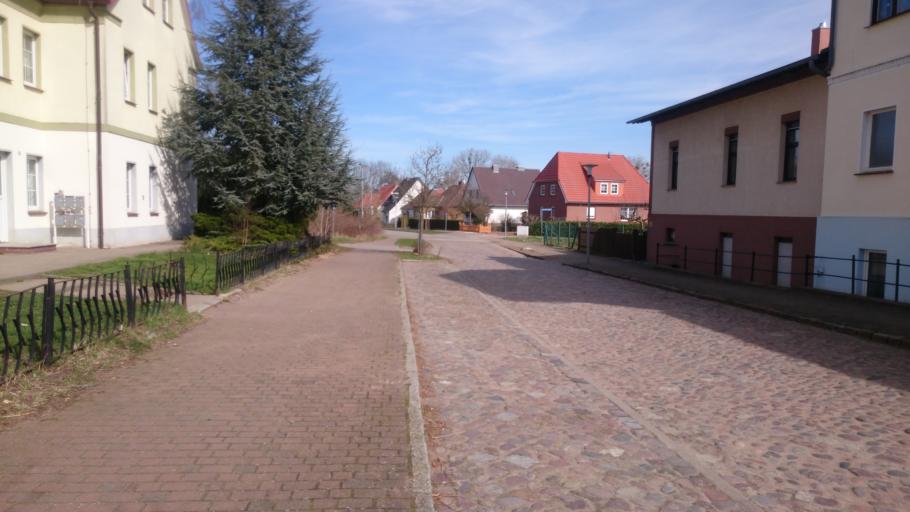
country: DE
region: Mecklenburg-Vorpommern
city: Teterow
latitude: 53.7811
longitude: 12.5757
